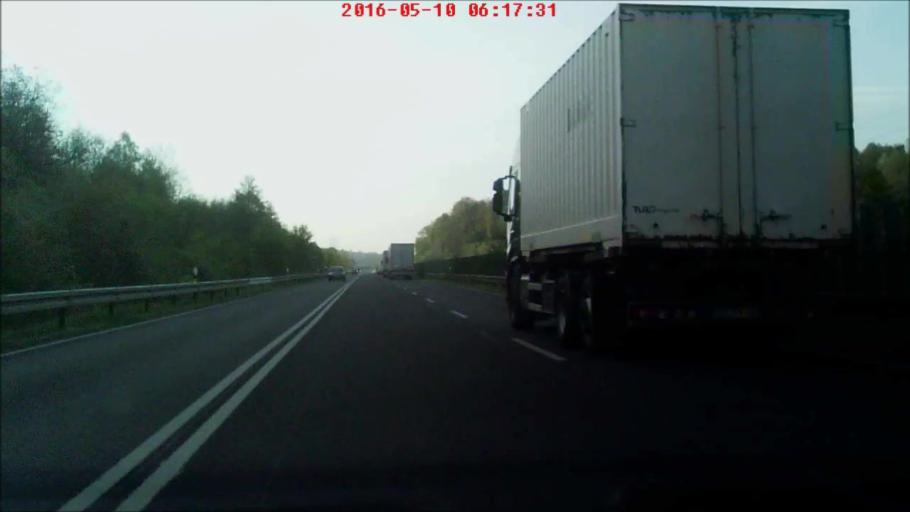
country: DE
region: Hesse
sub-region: Regierungsbezirk Kassel
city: Burghaun
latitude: 50.7335
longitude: 9.6962
